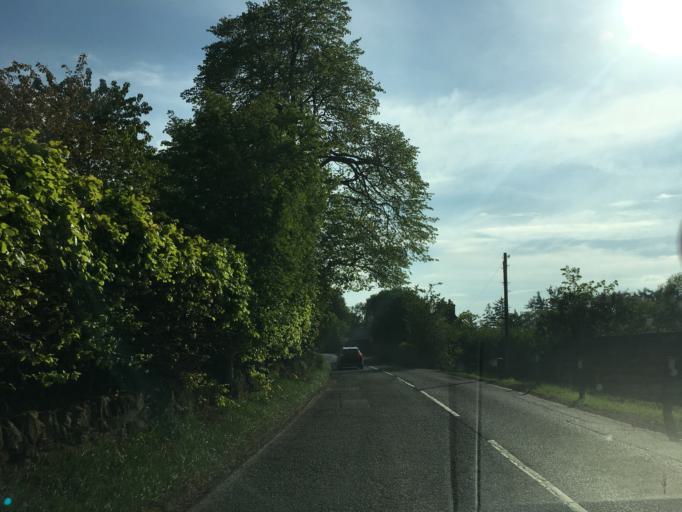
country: GB
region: Scotland
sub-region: The Scottish Borders
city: West Linton
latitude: 55.7254
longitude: -3.3261
